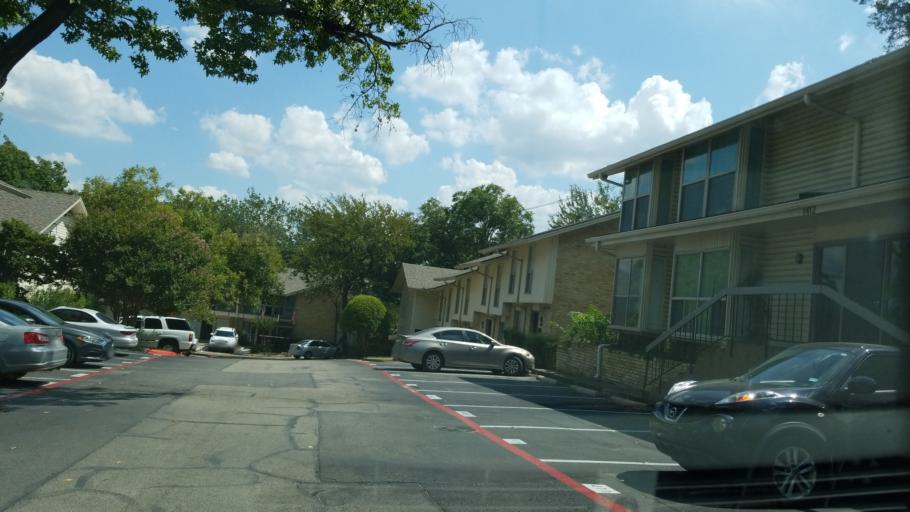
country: US
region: Texas
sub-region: Dallas County
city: Cockrell Hill
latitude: 32.7625
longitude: -96.8489
